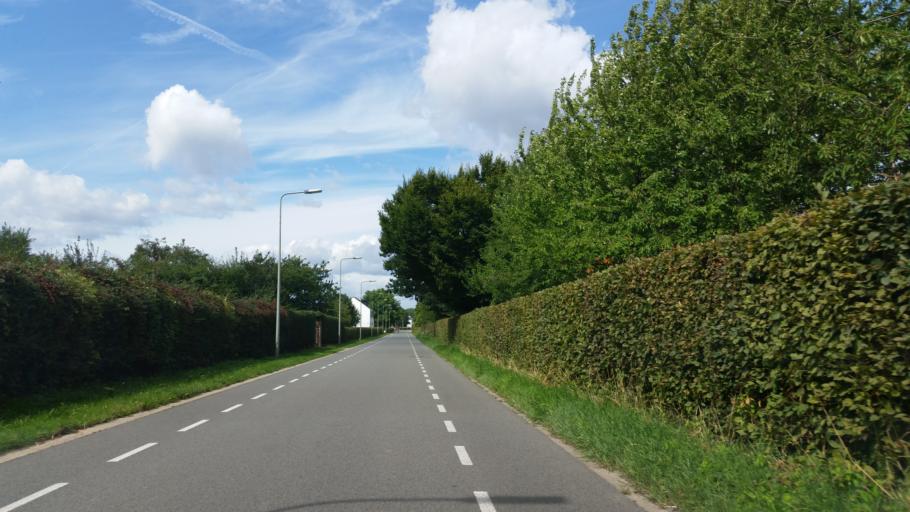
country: NL
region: Limburg
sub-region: Gemeente Maastricht
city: Heer
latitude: 50.8469
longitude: 5.7449
